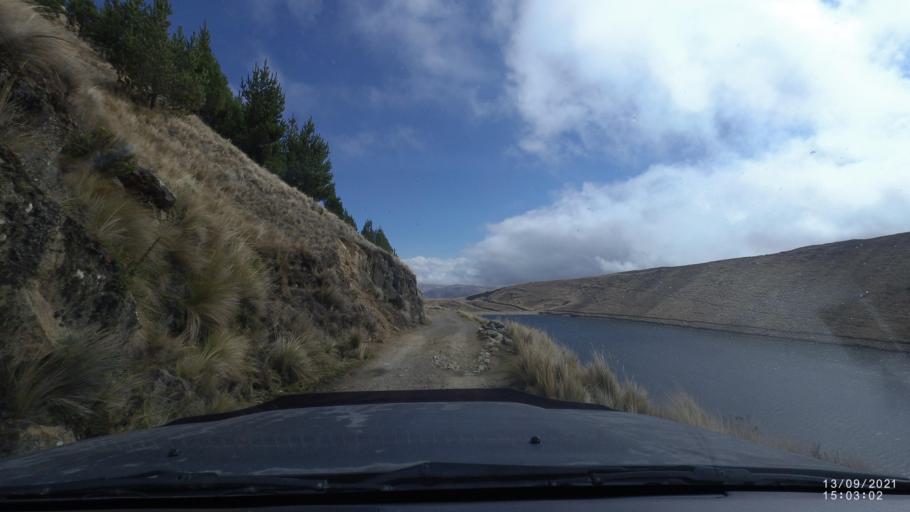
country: BO
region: Cochabamba
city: Colomi
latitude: -17.3335
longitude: -65.7903
